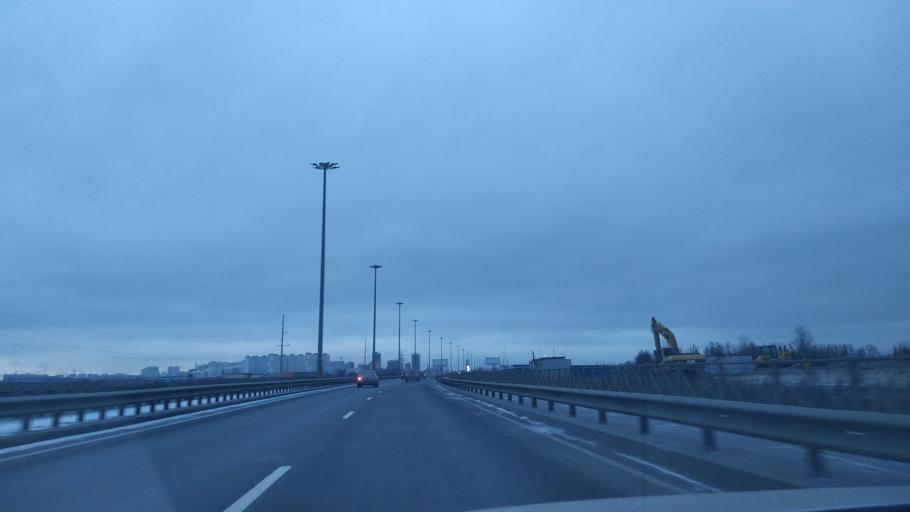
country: RU
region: St.-Petersburg
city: Shushary
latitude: 59.7847
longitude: 30.3950
